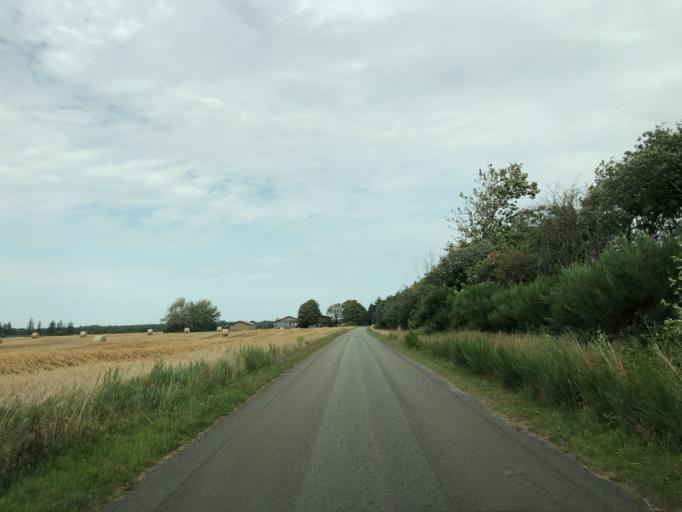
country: DK
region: Central Jutland
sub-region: Holstebro Kommune
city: Ulfborg
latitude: 56.2111
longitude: 8.3176
